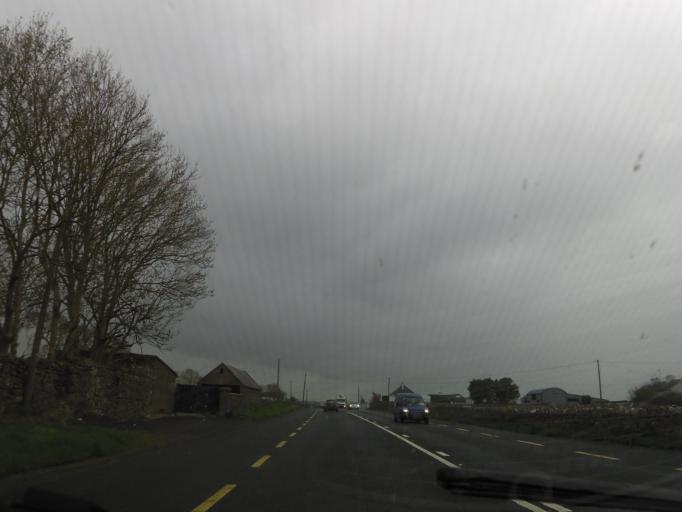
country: IE
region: Connaught
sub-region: County Galway
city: Tuam
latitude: 53.4990
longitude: -8.8885
